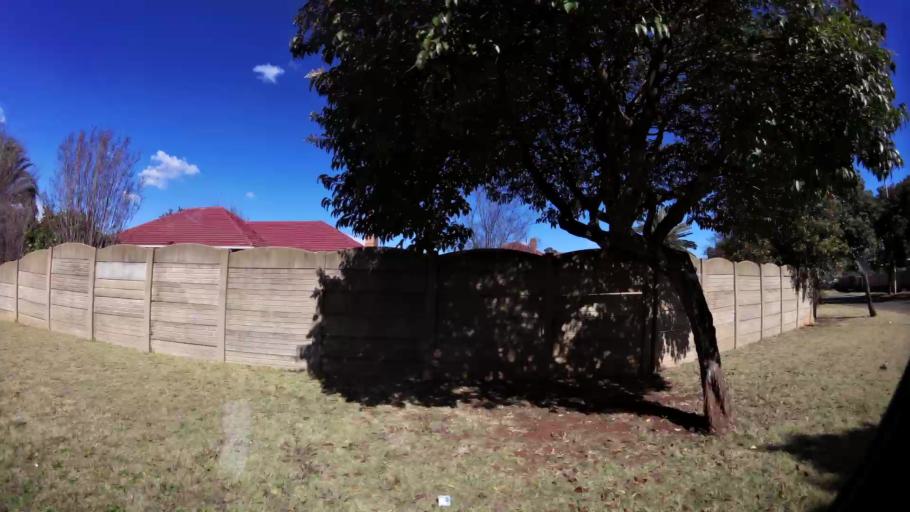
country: ZA
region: Gauteng
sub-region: West Rand District Municipality
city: Carletonville
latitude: -26.3609
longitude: 27.3957
